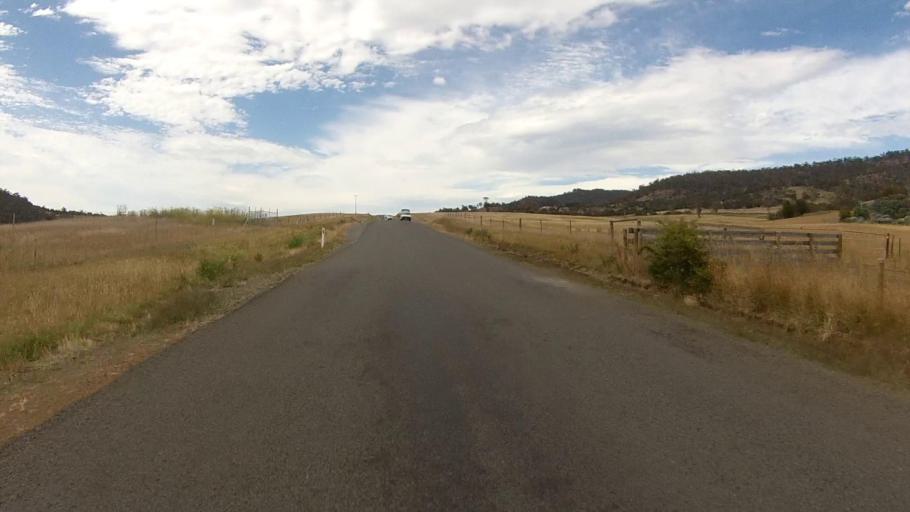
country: AU
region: Tasmania
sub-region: Brighton
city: Old Beach
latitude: -42.7308
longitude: 147.3481
